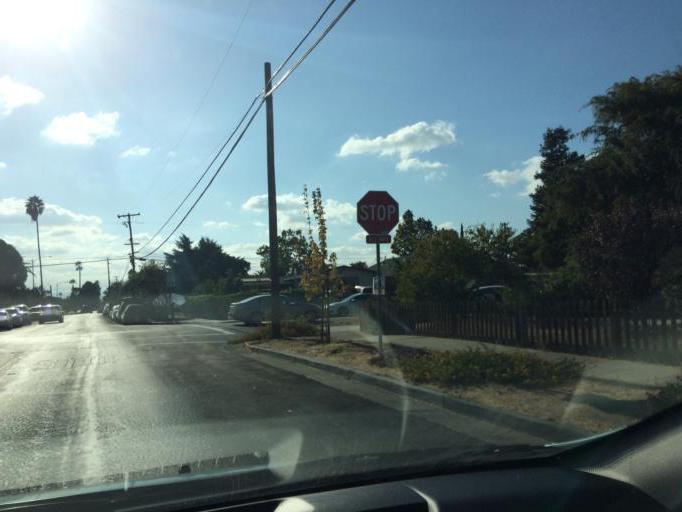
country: US
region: California
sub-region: Santa Clara County
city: Alum Rock
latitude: 37.3274
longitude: -121.8268
